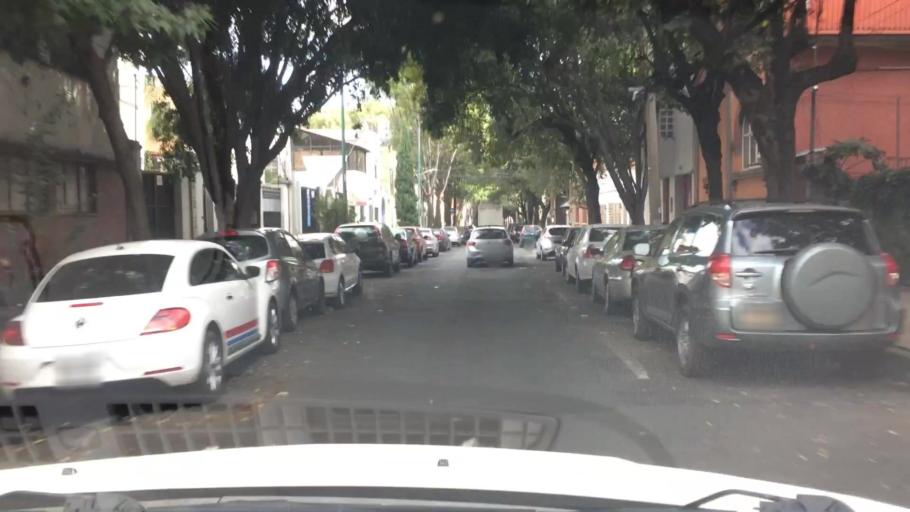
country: MX
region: Mexico City
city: Polanco
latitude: 19.4039
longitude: -99.1831
